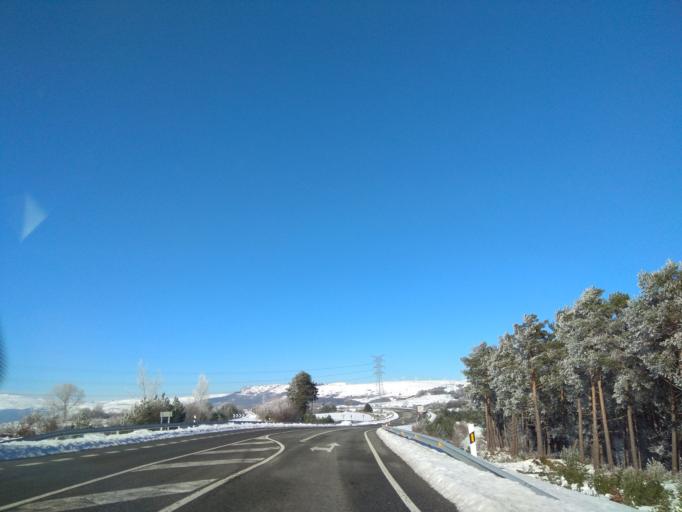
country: ES
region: Castille and Leon
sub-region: Provincia de Burgos
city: Arija
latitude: 43.0031
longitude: -3.8421
